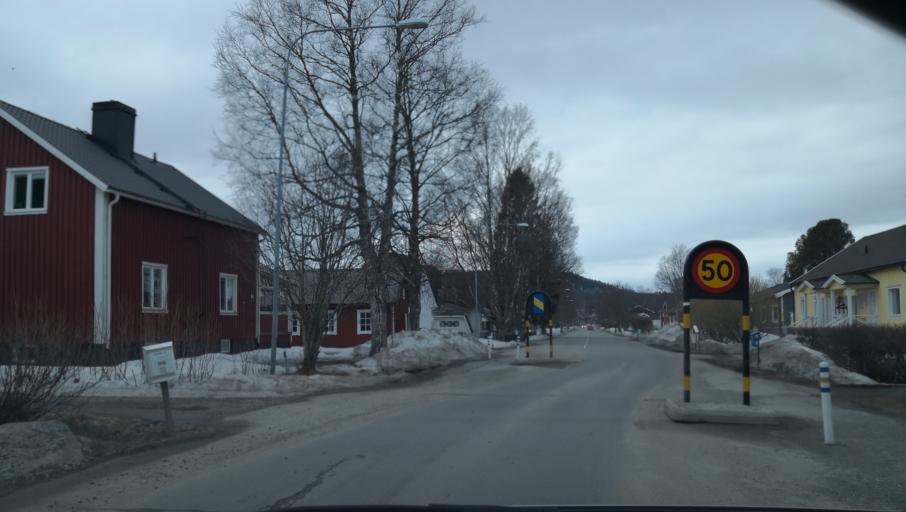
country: SE
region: Vaesterbotten
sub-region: Vannas Kommun
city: Vannasby
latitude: 63.9142
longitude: 19.8345
